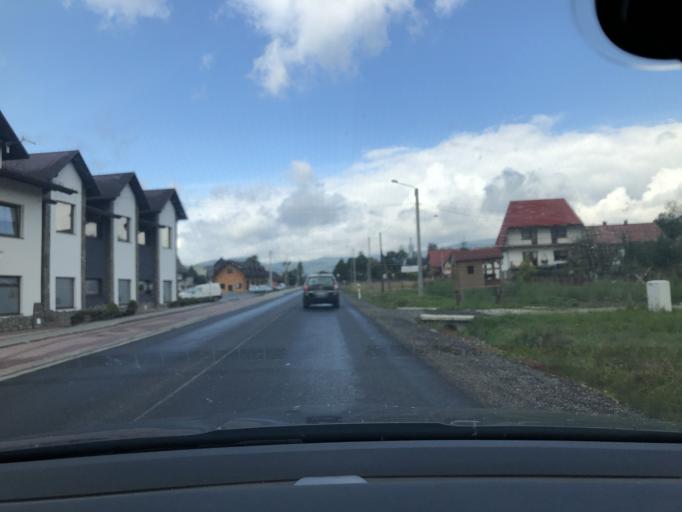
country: PL
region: Lesser Poland Voivodeship
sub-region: Powiat nowotarski
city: Zubrzyca Gorna
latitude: 49.5473
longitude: 19.6612
